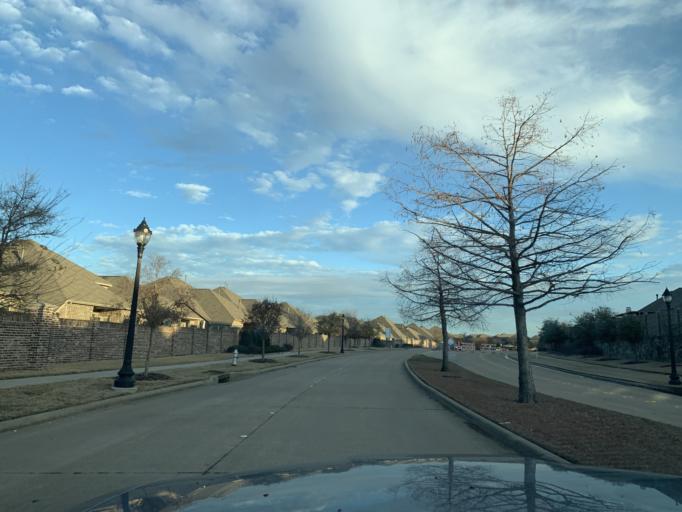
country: US
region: Texas
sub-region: Tarrant County
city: Euless
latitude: 32.8465
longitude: -97.0703
